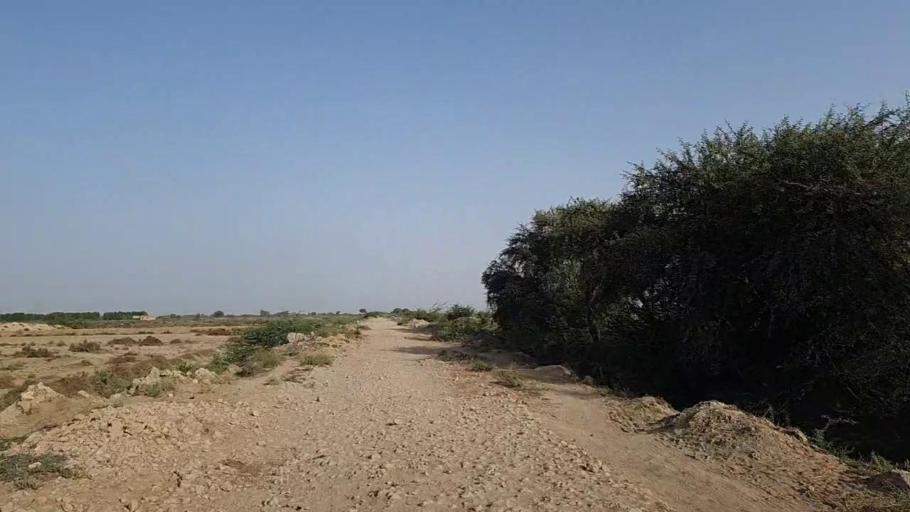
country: PK
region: Sindh
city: Jati
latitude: 24.2619
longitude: 68.1735
